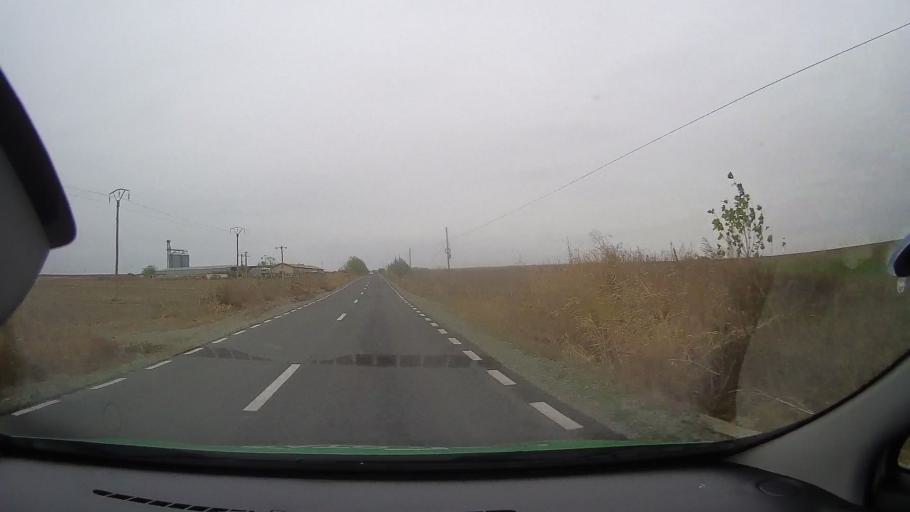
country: RO
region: Constanta
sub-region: Comuna Tortoman
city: Tortoman
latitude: 44.3618
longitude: 28.2098
